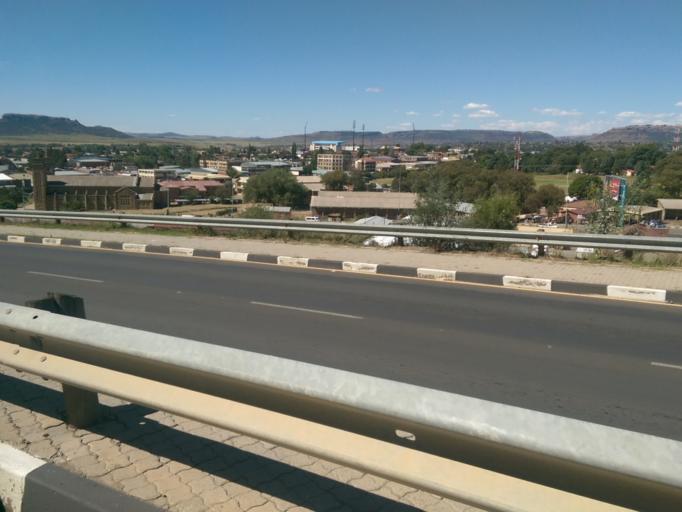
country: LS
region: Maseru
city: Maseru
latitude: -29.3194
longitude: 27.4941
